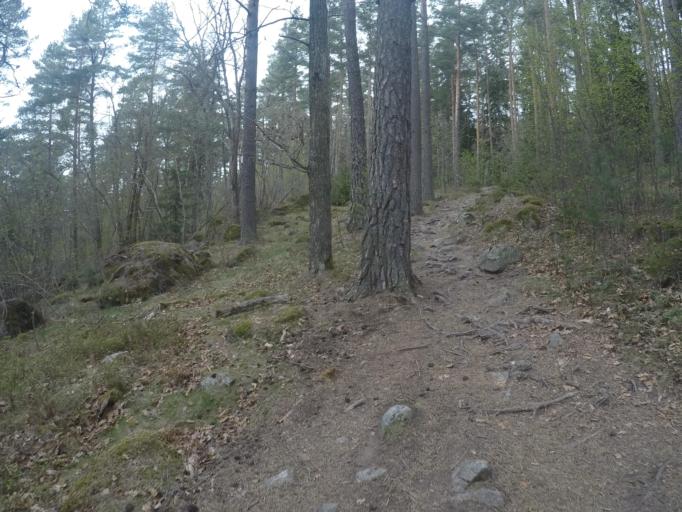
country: SE
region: Vaestmanland
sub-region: Vasteras
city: Vasteras
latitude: 59.6243
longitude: 16.5218
